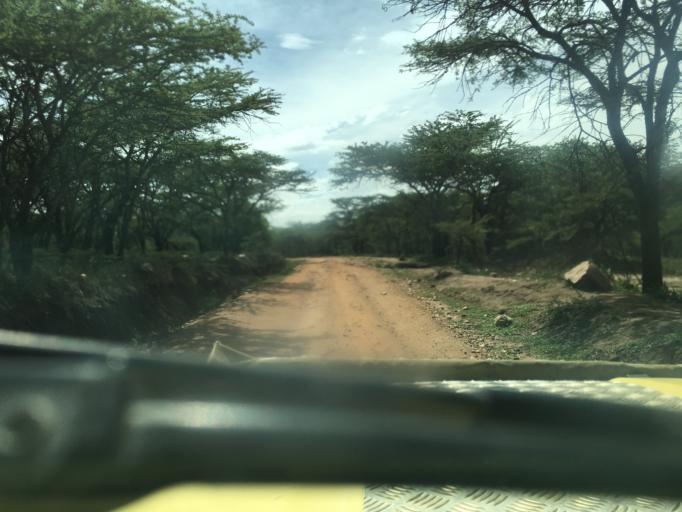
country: TZ
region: Mara
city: Mugumu
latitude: -1.8906
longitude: 35.2770
